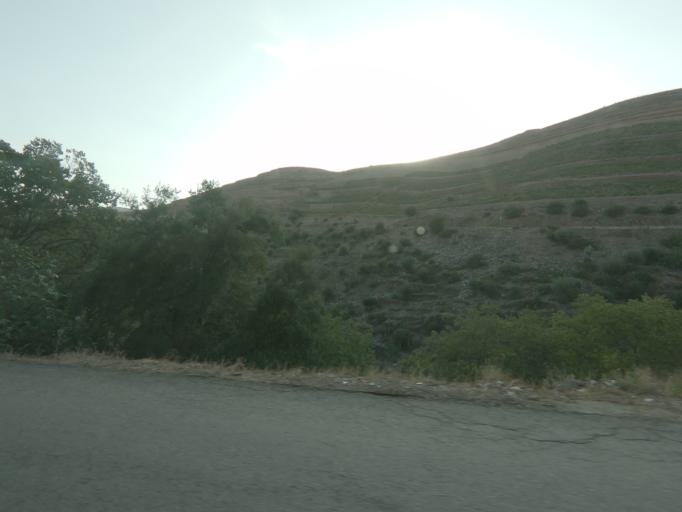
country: PT
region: Vila Real
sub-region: Sabrosa
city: Vilela
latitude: 41.1670
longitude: -7.6247
